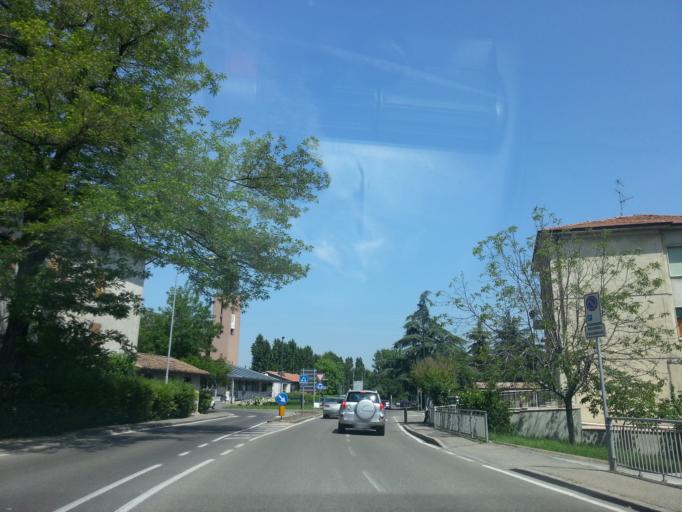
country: IT
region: Emilia-Romagna
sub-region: Provincia di Reggio Emilia
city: Fogliano
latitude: 44.6729
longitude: 10.6384
